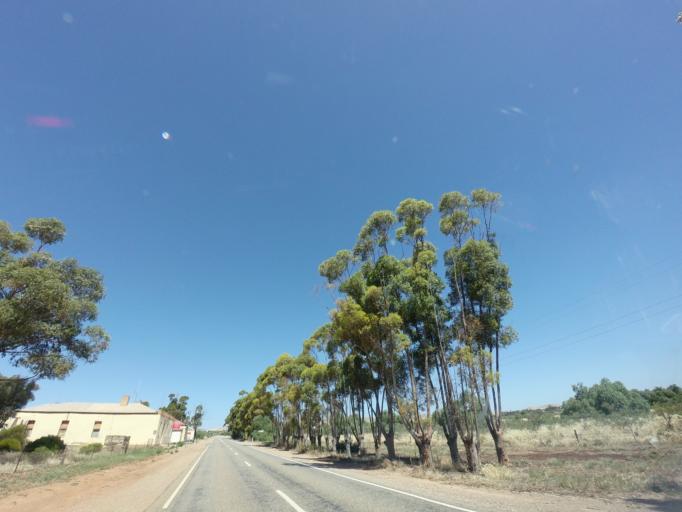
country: AU
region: South Australia
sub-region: Peterborough
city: Peterborough
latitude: -32.7204
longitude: 138.4923
